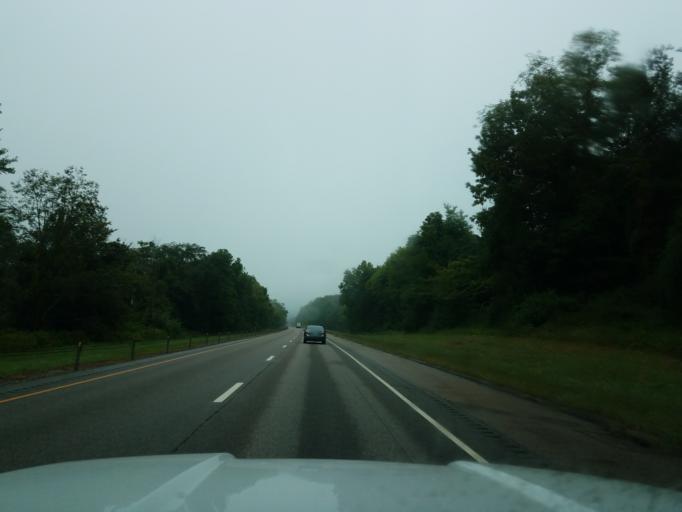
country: US
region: Connecticut
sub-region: New London County
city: Colchester
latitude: 41.5701
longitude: -72.2878
